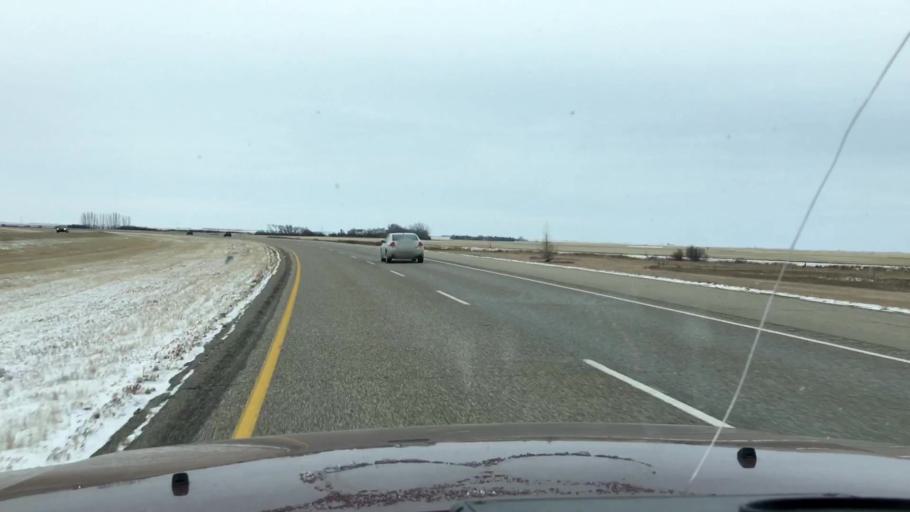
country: CA
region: Saskatchewan
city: Watrous
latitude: 51.1474
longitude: -105.9071
